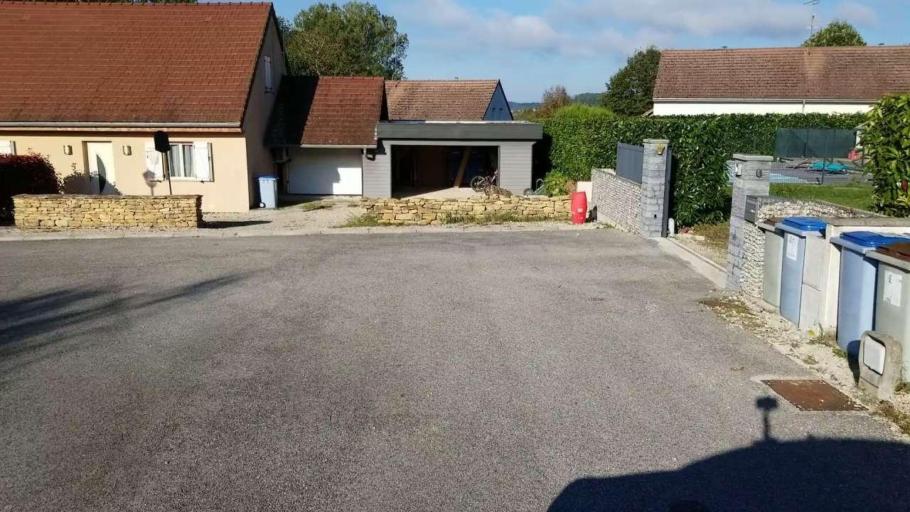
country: FR
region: Franche-Comte
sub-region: Departement du Jura
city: Poligny
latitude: 46.7990
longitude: 5.6135
